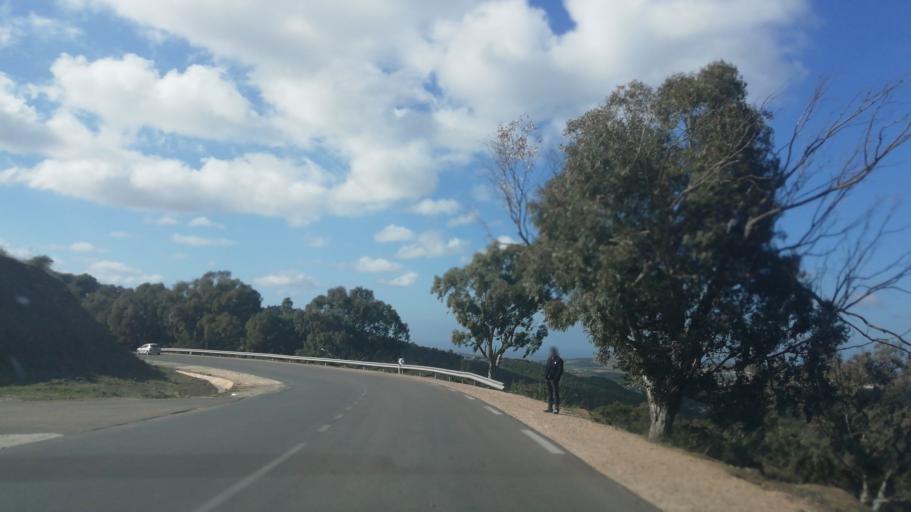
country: DZ
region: Relizane
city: Relizane
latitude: 36.0901
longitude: 0.4734
